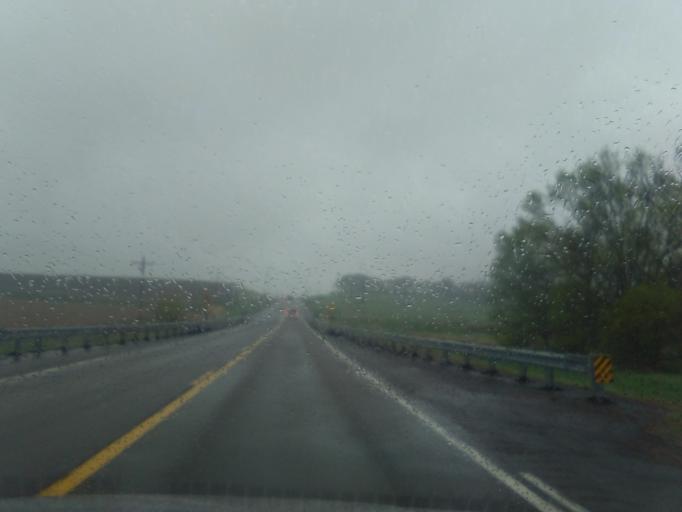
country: US
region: Nebraska
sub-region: Wayne County
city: Wayne
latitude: 42.2354
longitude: -97.1705
